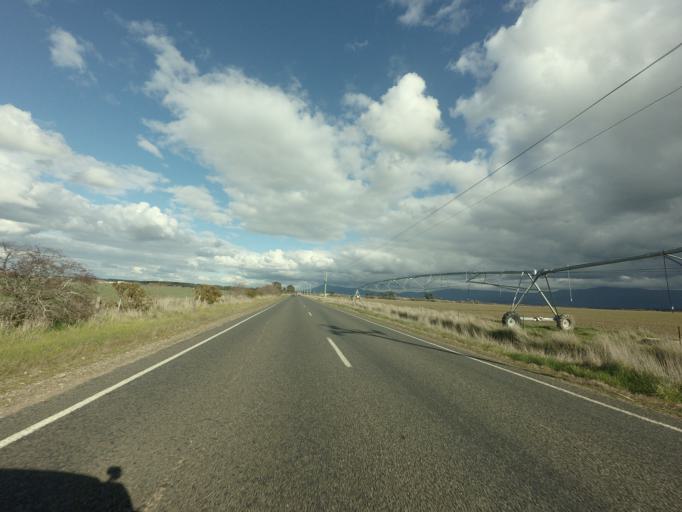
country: AU
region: Tasmania
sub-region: Northern Midlands
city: Longford
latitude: -41.7054
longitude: 147.0761
